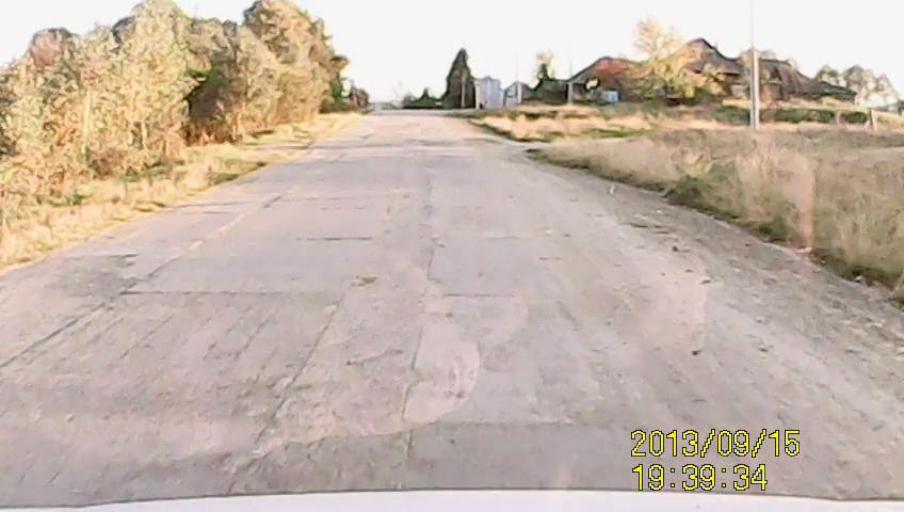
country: RU
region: Chelyabinsk
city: Kyshtym
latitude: 55.8513
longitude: 60.4815
